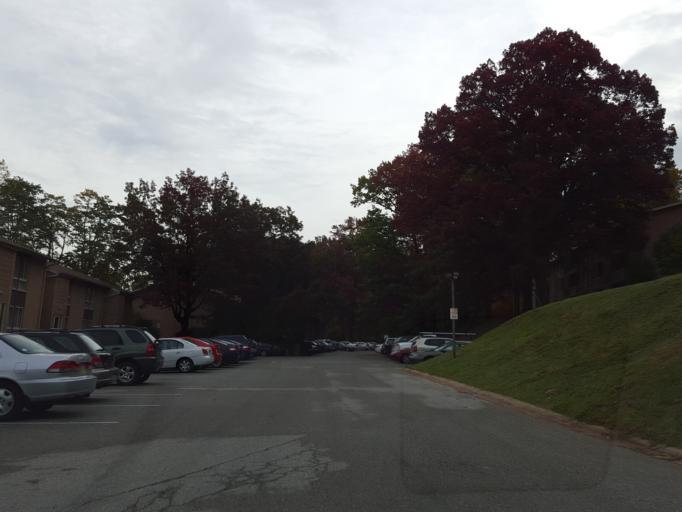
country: US
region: Pennsylvania
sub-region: York County
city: Valley View
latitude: 39.9411
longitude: -76.6892
